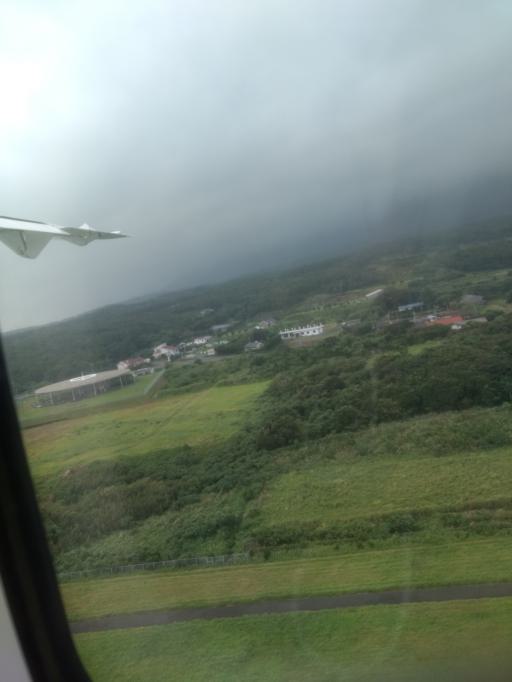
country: JP
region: Kagoshima
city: Nishinoomote
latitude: 30.3840
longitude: 130.6618
